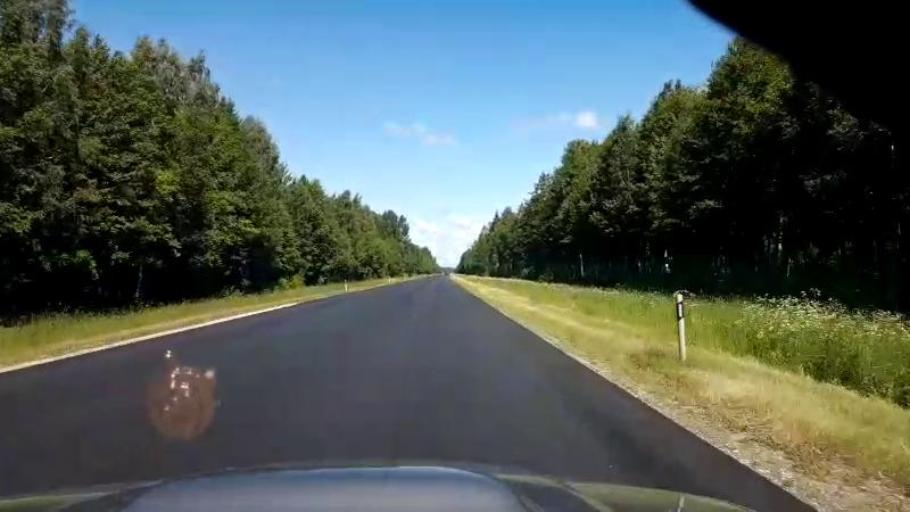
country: LV
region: Salacgrivas
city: Ainazi
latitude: 57.9503
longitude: 24.4369
